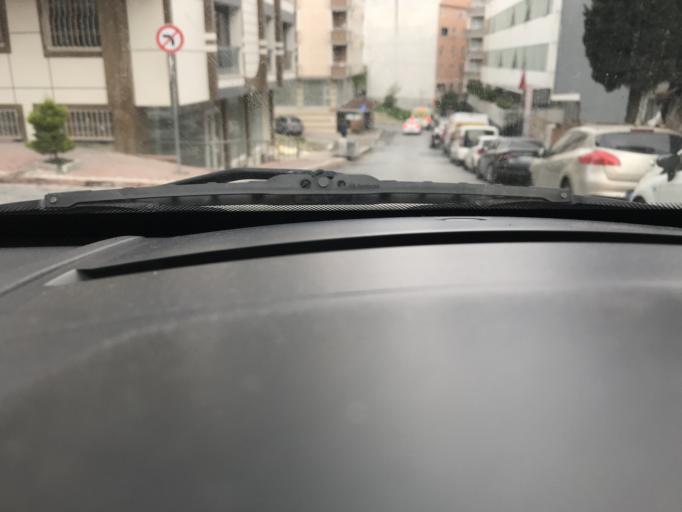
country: TR
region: Istanbul
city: Yakuplu
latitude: 41.0032
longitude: 28.6982
